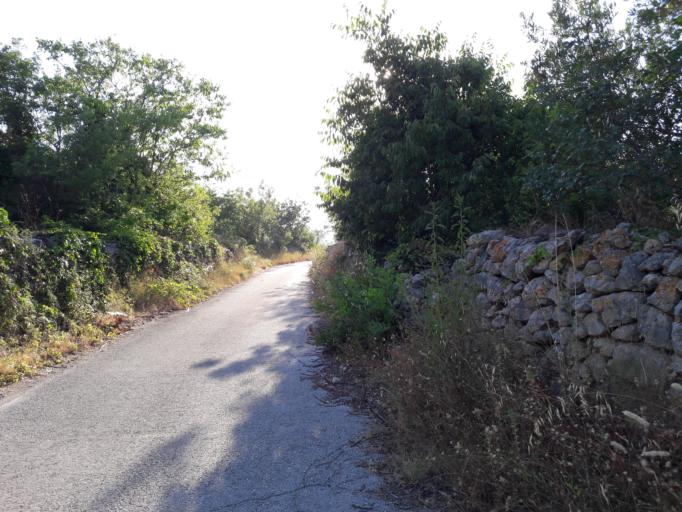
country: HR
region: Sibensko-Kniniska
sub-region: Grad Sibenik
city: Sibenik
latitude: 43.6945
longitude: 15.8447
